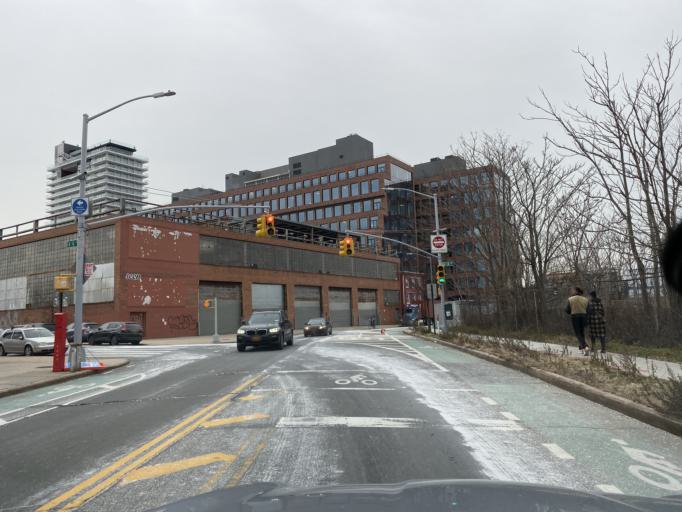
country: US
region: New York
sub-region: Queens County
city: Long Island City
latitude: 40.7245
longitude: -73.9578
